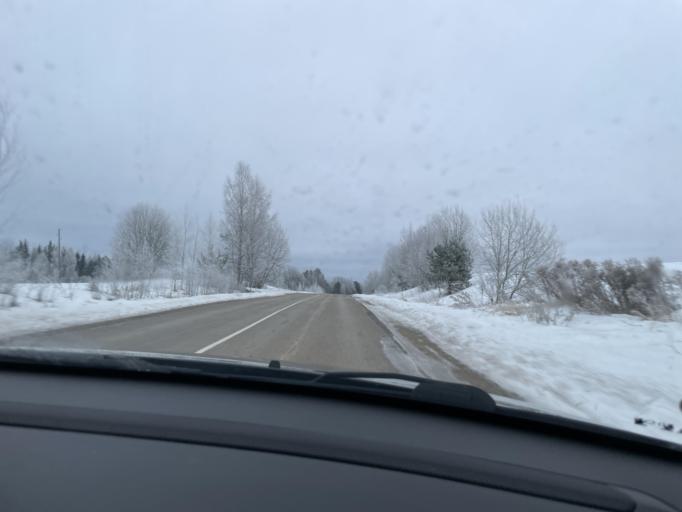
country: LV
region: Rezekne
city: Rezekne
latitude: 56.4381
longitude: 27.5223
